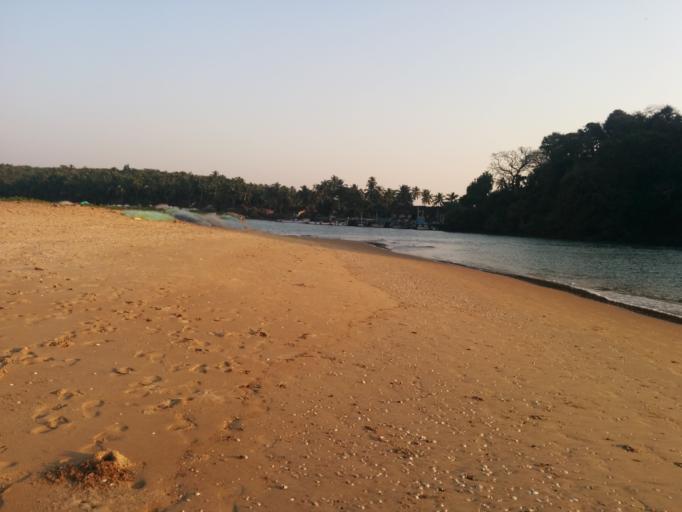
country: IN
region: Karnataka
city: Canacona
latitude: 14.9850
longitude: 74.0386
